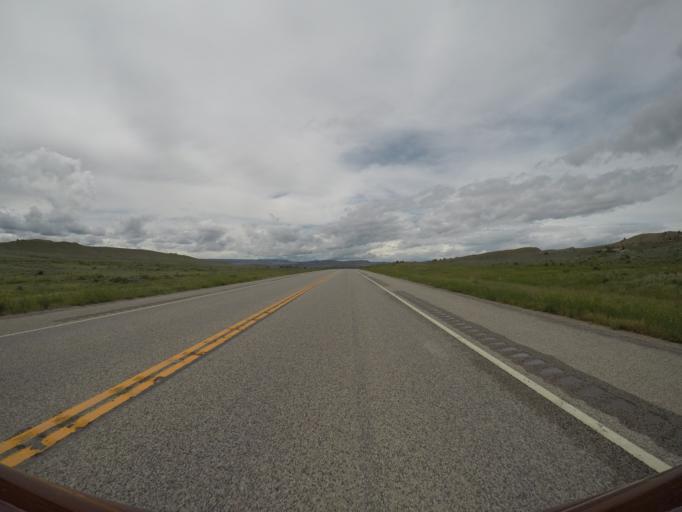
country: US
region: Montana
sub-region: Carbon County
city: Red Lodge
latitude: 45.2196
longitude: -108.8790
